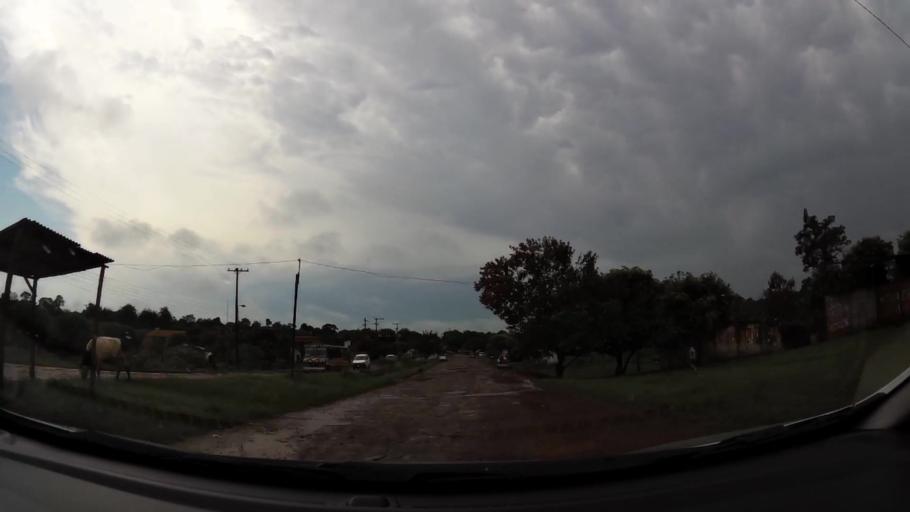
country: PY
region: Alto Parana
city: Presidente Franco
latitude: -25.5323
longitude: -54.6691
